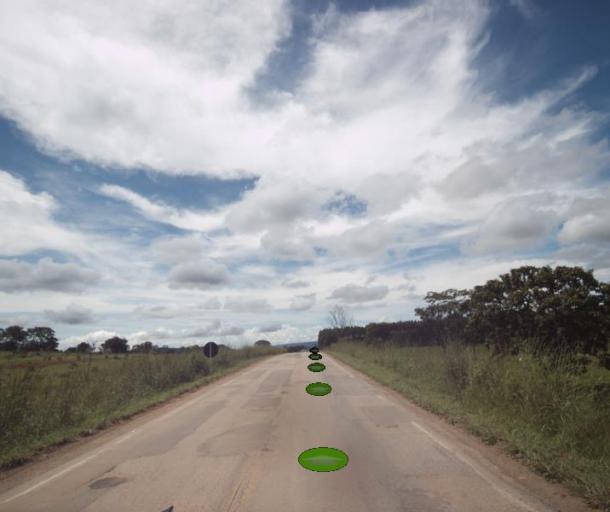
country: BR
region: Goias
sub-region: Padre Bernardo
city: Padre Bernardo
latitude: -15.5034
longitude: -48.2065
